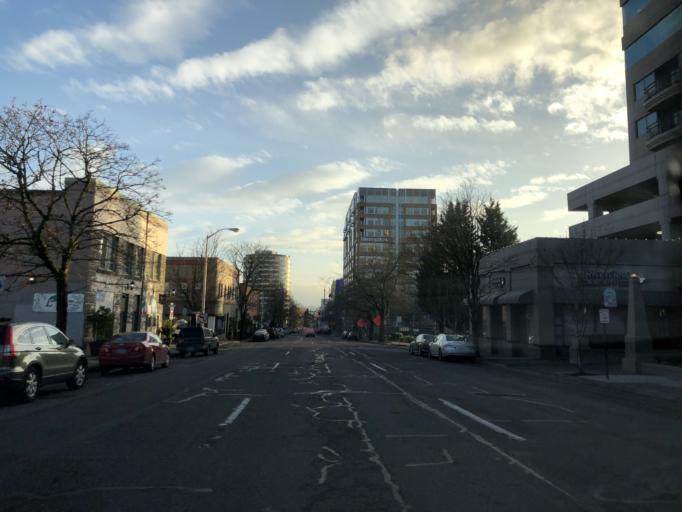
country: US
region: Washington
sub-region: Clark County
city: Vancouver
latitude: 45.6285
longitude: -122.6727
